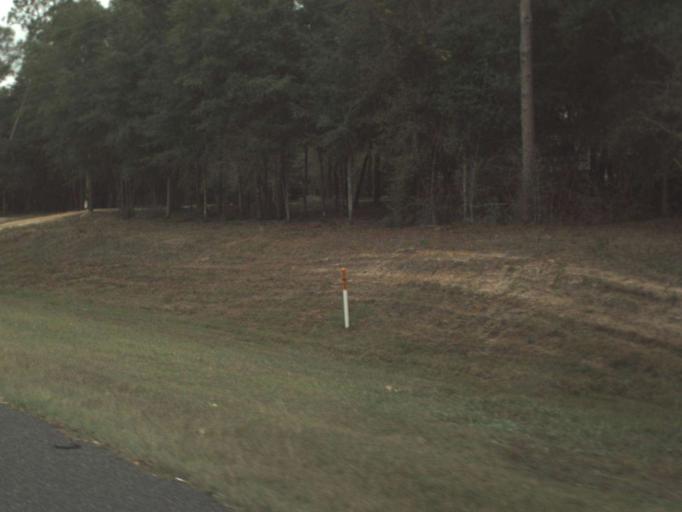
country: US
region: Florida
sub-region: Escambia County
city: Century
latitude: 30.8850
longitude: -87.3215
